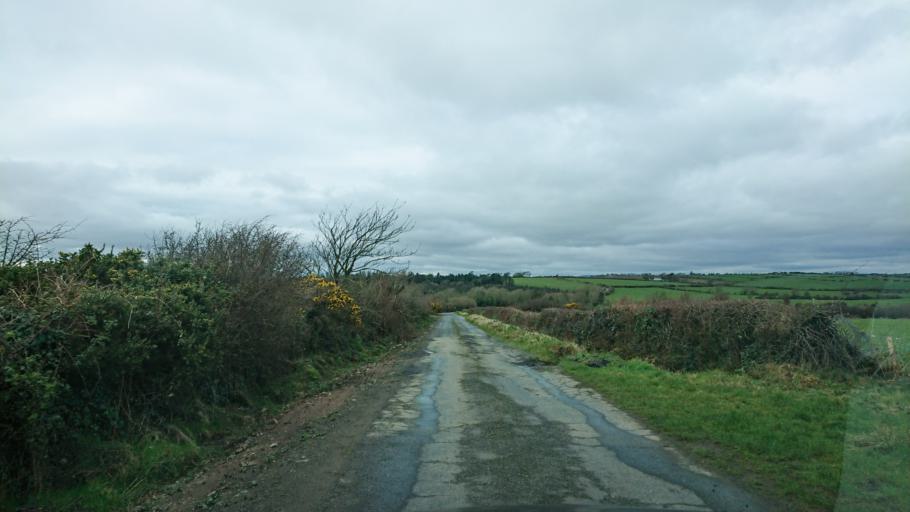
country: IE
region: Munster
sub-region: Waterford
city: Dunmore East
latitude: 52.1642
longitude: -7.0366
